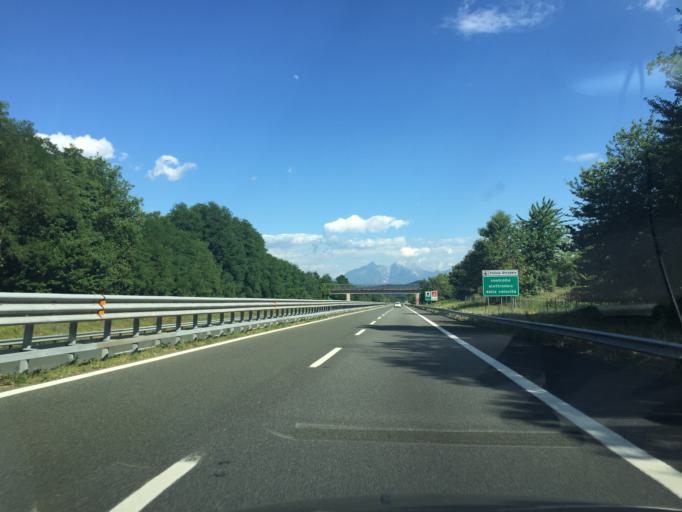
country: IT
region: Tuscany
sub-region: Provincia di Massa-Carrara
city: Filattiera
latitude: 44.3249
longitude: 9.9143
